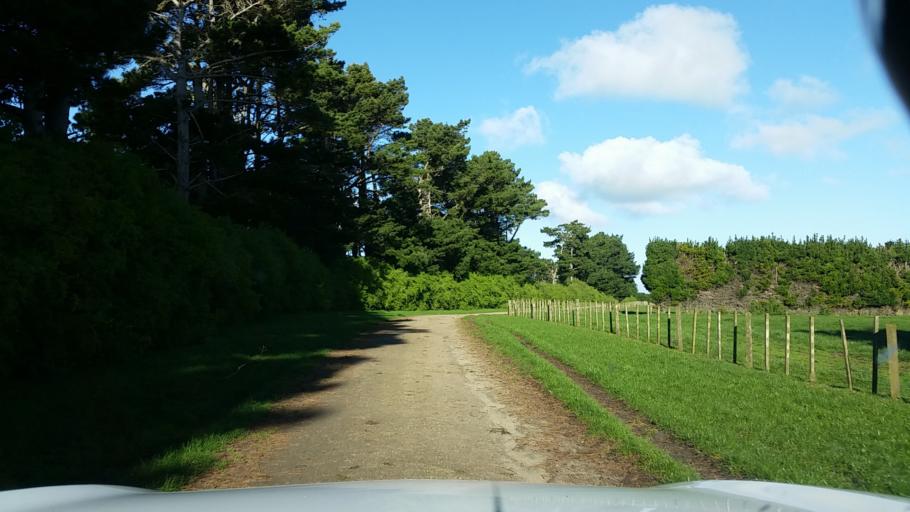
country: NZ
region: Taranaki
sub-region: South Taranaki District
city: Patea
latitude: -39.7397
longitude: 174.5429
